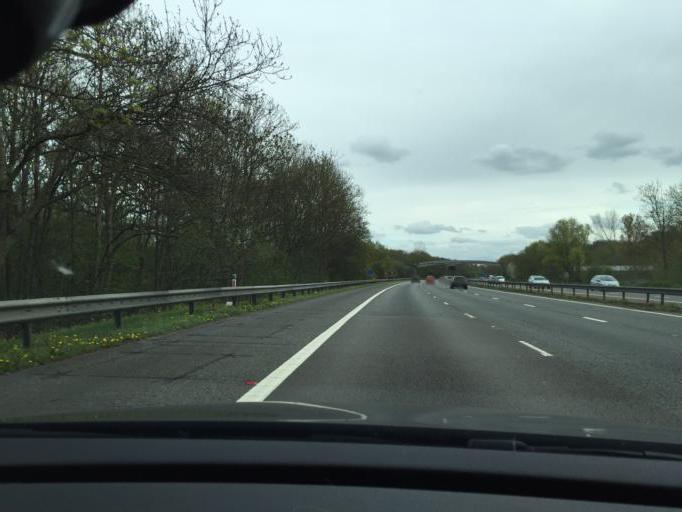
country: GB
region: England
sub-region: West Berkshire
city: Theale
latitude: 51.4539
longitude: -1.0813
